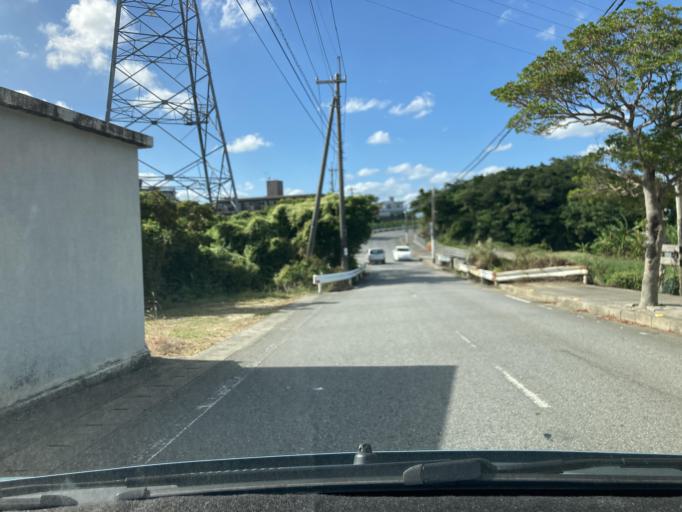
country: JP
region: Okinawa
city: Gushikawa
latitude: 26.3680
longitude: 127.8421
